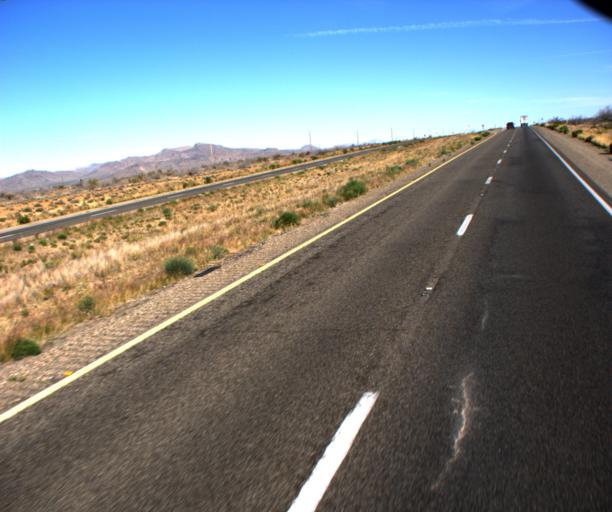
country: US
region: Arizona
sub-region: Mohave County
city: Golden Valley
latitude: 35.3069
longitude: -114.1940
